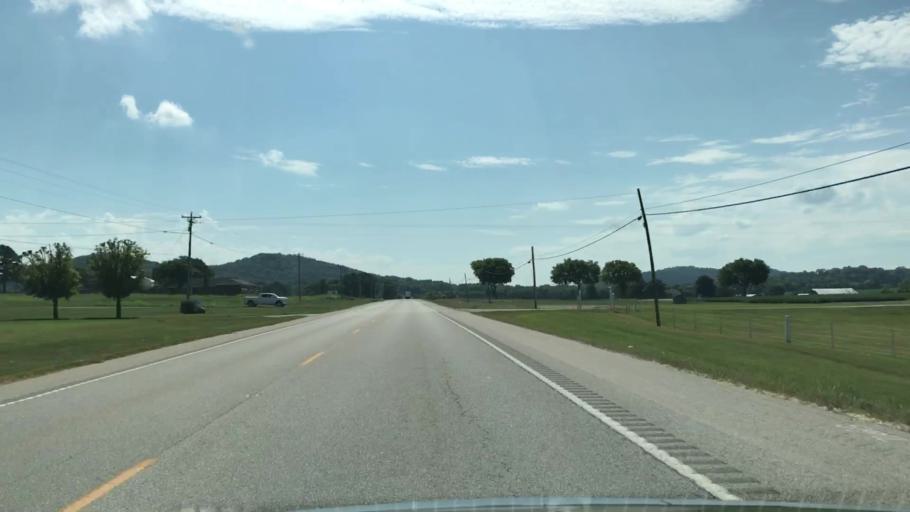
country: US
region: Tennessee
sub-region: Smith County
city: Carthage
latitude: 36.3408
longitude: -86.0327
